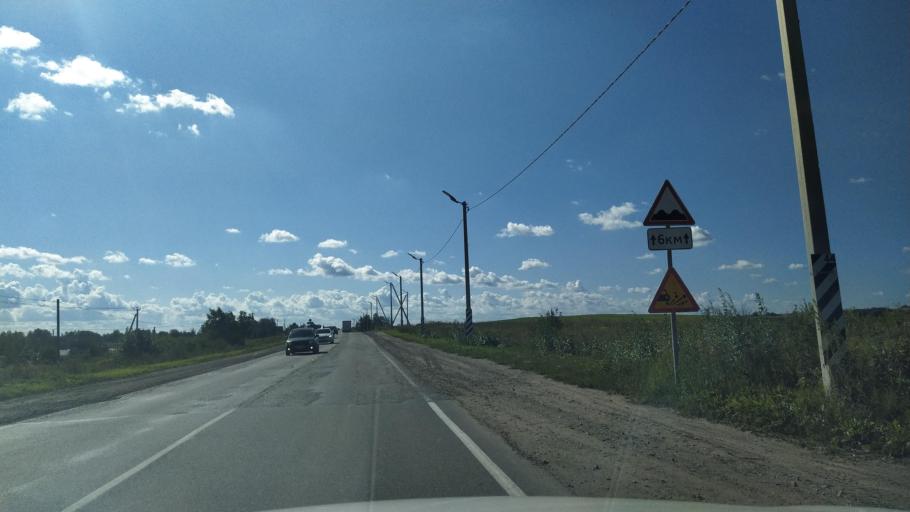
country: RU
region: Leningrad
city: Kommunar
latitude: 59.6015
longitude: 30.3211
